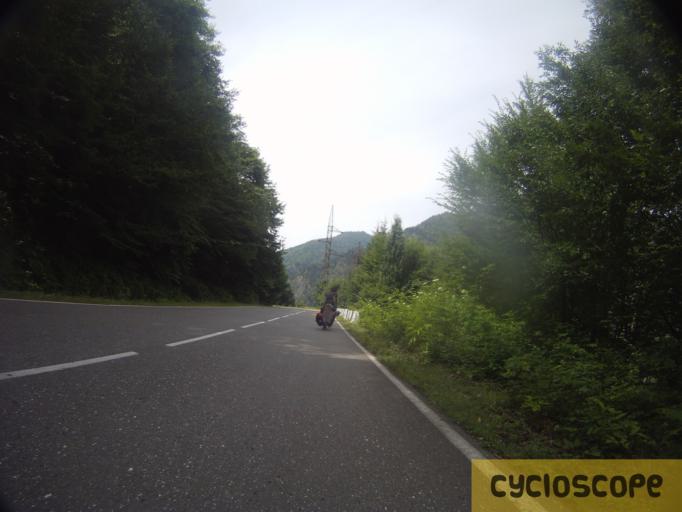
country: GE
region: Samegrelo and Zemo Svaneti
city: Jvari
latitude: 42.9131
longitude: 42.0722
